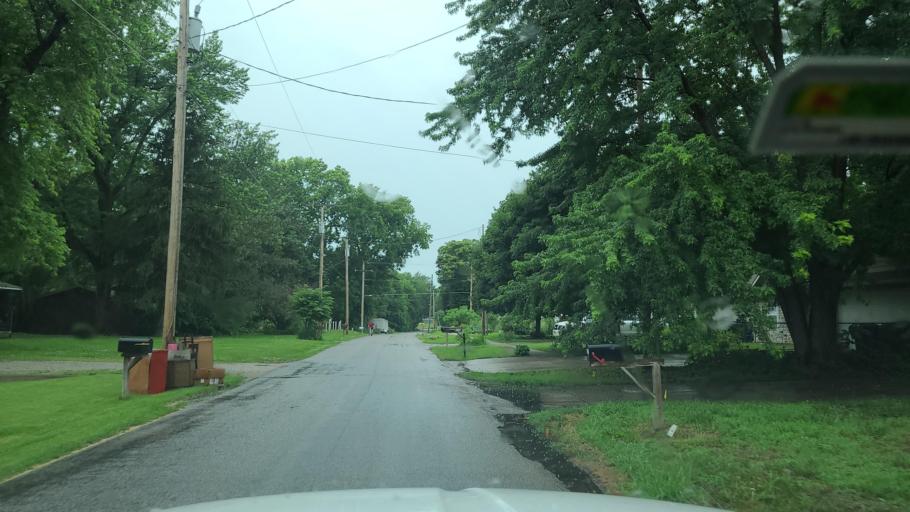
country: US
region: Kansas
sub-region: Douglas County
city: Lawrence
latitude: 38.9751
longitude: -95.2277
